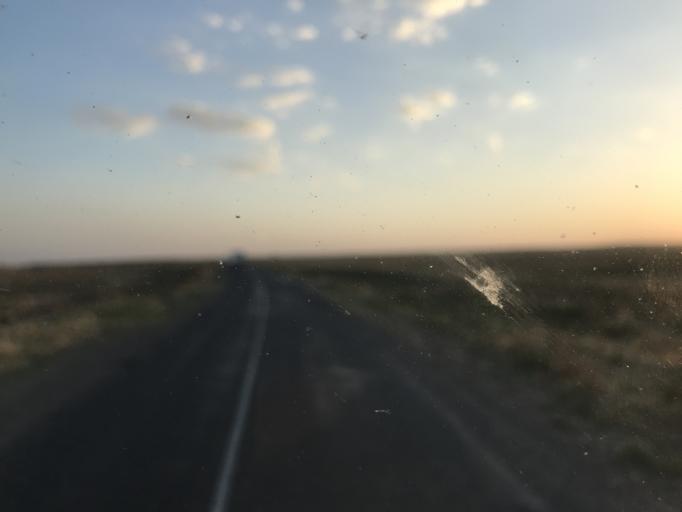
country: UZ
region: Toshkent
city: Yangiyul
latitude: 41.3836
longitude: 68.7635
